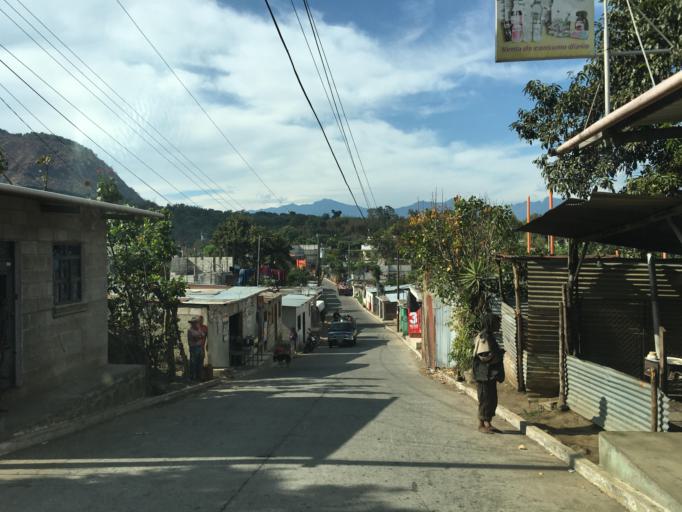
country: GT
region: Solola
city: San Antonio Palopo
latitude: 14.6624
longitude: -91.1629
